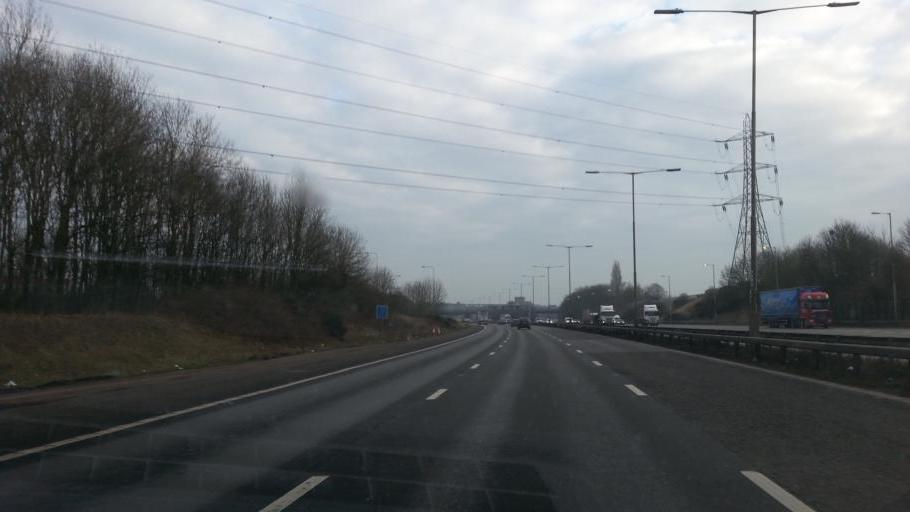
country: GB
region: England
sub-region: Solihull
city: Chelmsley Wood
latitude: 52.4814
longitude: -1.7205
